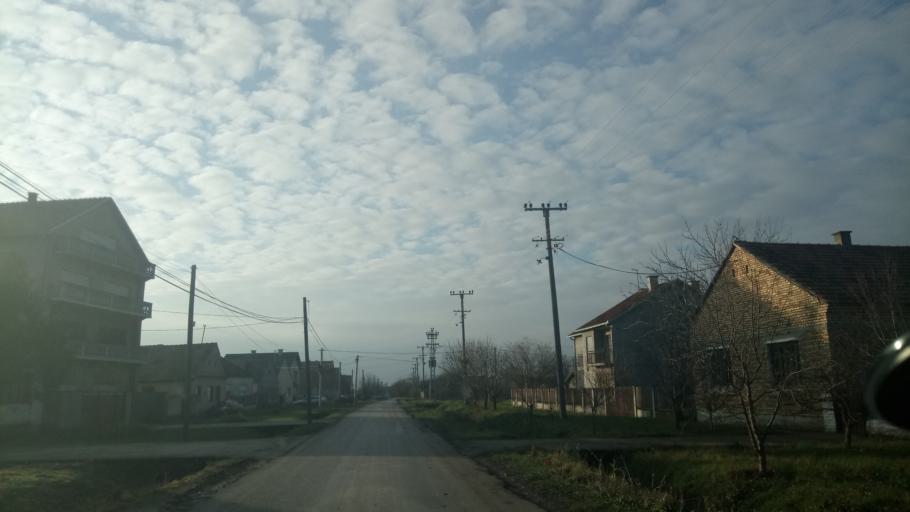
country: RS
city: Vojka
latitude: 44.9306
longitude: 20.1487
